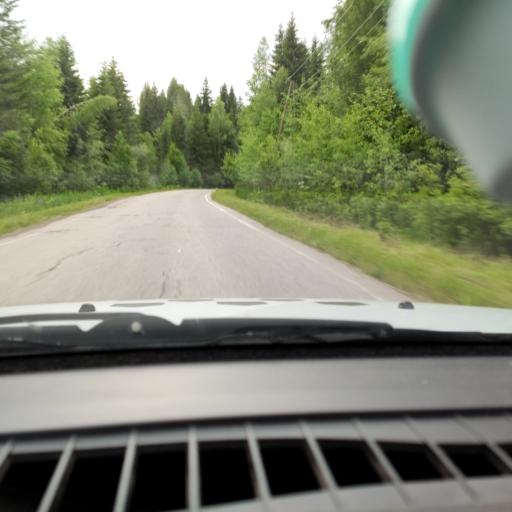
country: RU
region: Perm
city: Lys'va
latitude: 58.1150
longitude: 57.7000
